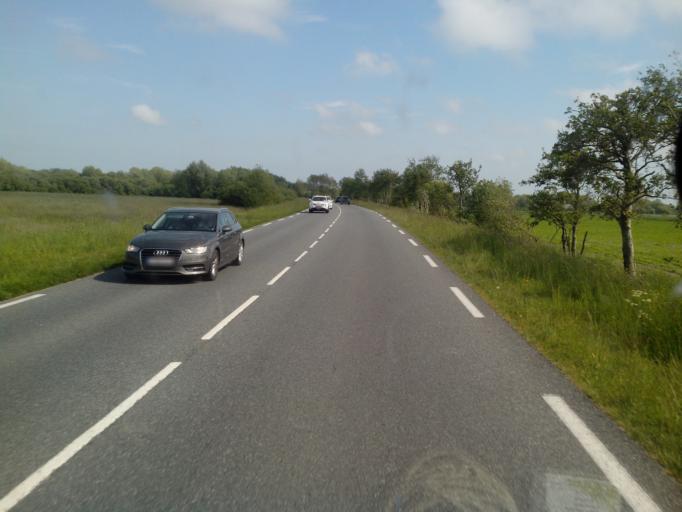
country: FR
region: Picardie
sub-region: Departement de la Somme
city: Rue
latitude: 50.2653
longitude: 1.6567
